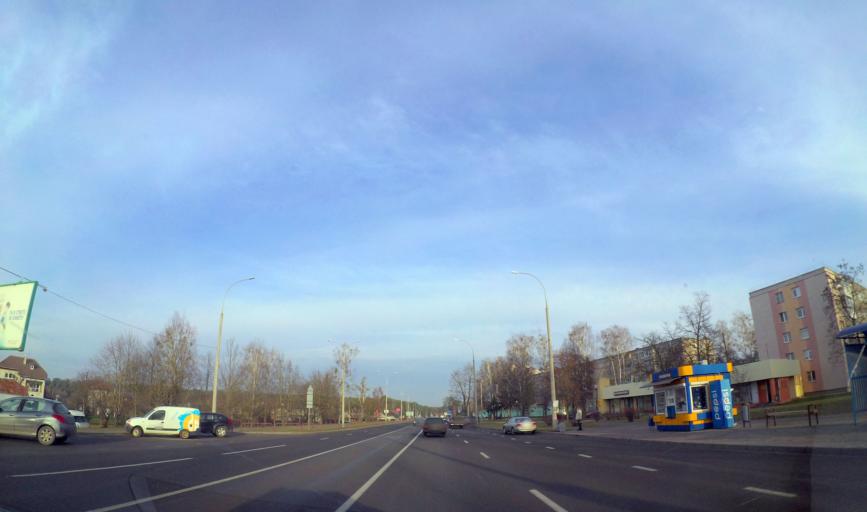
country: BY
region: Grodnenskaya
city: Hrodna
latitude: 53.6701
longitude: 23.7913
